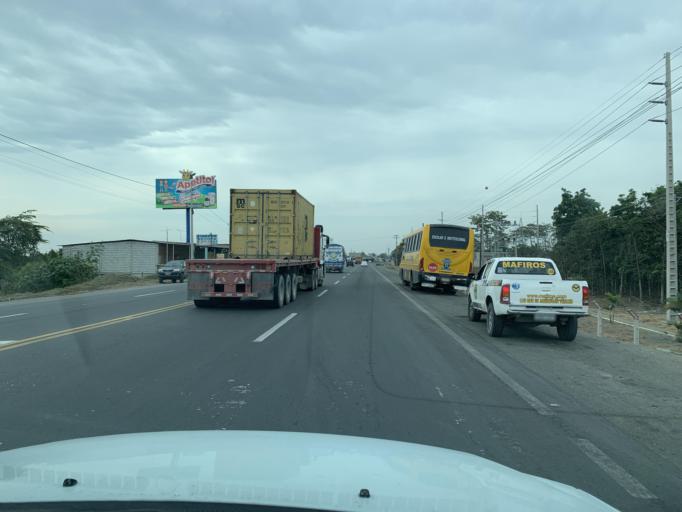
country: EC
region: Guayas
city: Yaguachi Nuevo
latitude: -2.2423
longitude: -79.6374
